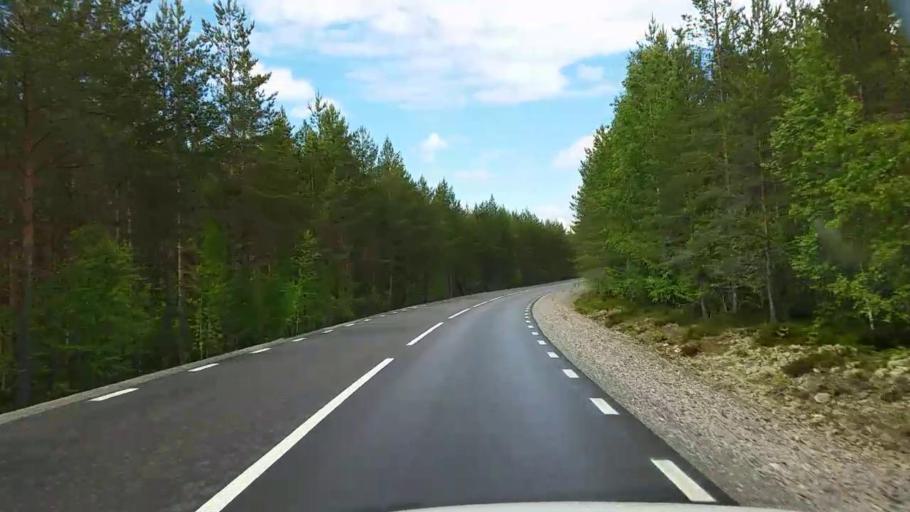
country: SE
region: Gaevleborg
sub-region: Sandvikens Kommun
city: Jarbo
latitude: 60.8799
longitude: 16.3870
